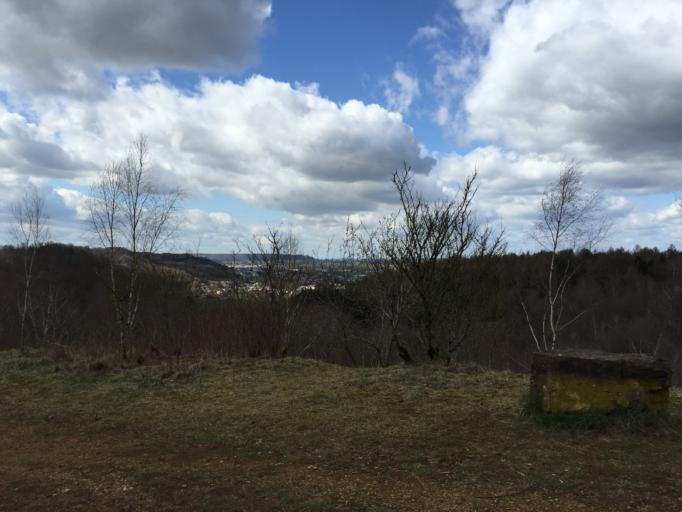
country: LU
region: Luxembourg
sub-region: Canton d'Esch-sur-Alzette
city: Petange
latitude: 49.5452
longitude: 5.8771
